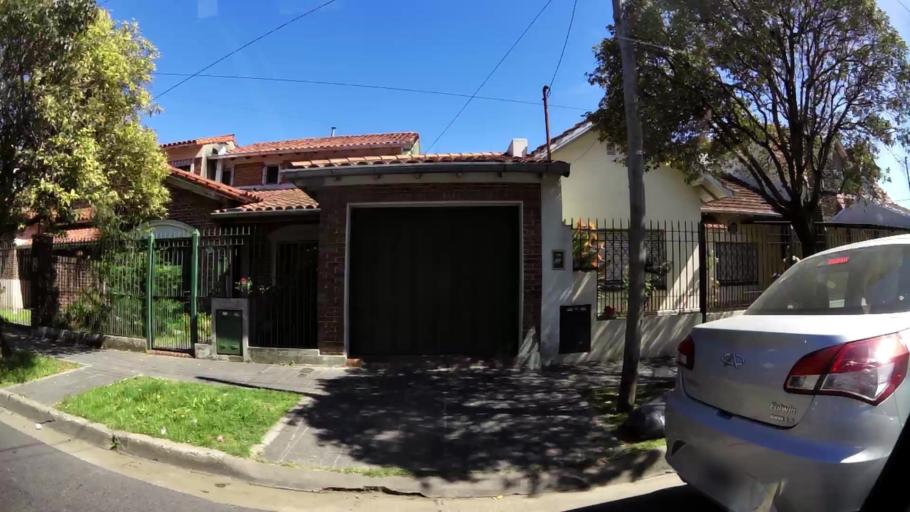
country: AR
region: Buenos Aires
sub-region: Partido de Vicente Lopez
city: Olivos
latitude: -34.5271
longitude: -58.5045
